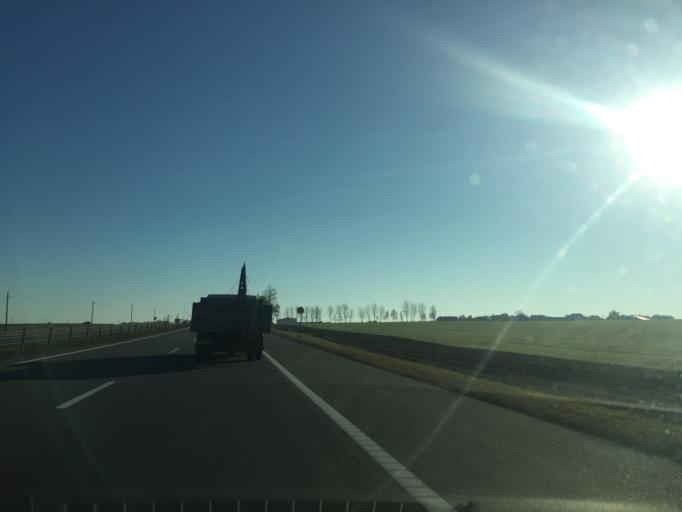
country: BY
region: Minsk
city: Luhavaya Slabada
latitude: 53.7615
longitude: 27.9046
